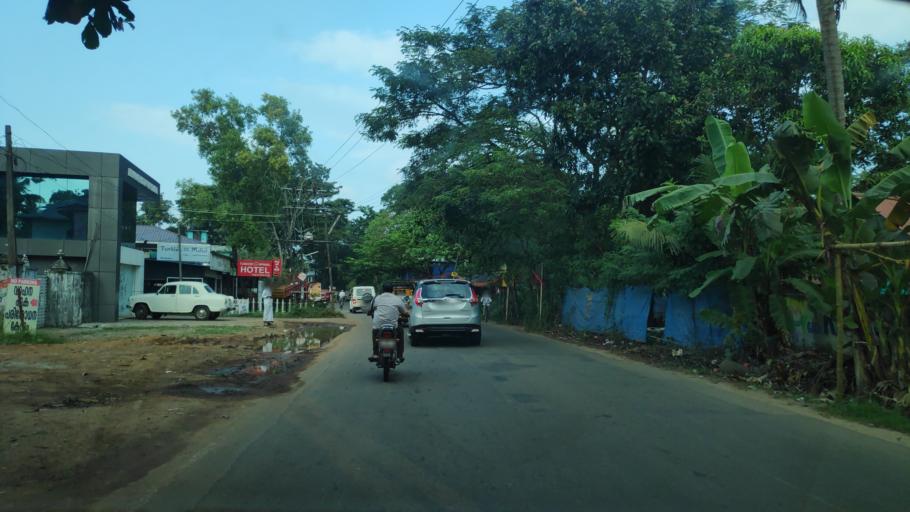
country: IN
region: Kerala
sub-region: Alappuzha
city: Alleppey
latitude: 9.5660
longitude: 76.3473
